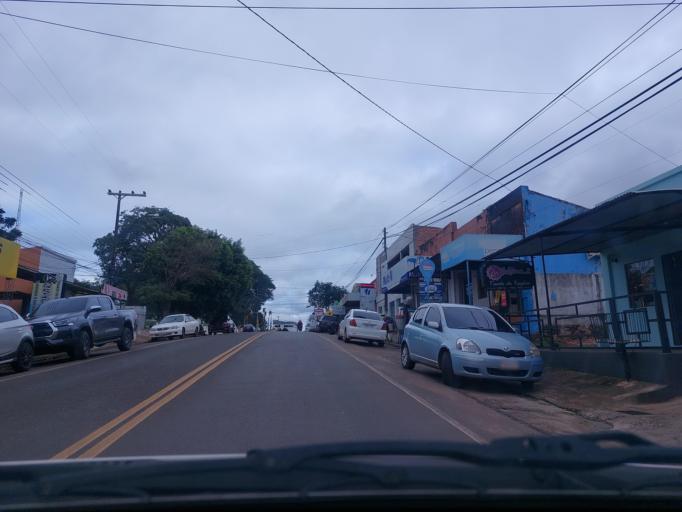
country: PY
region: San Pedro
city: Guayaybi
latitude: -24.6632
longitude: -56.4407
